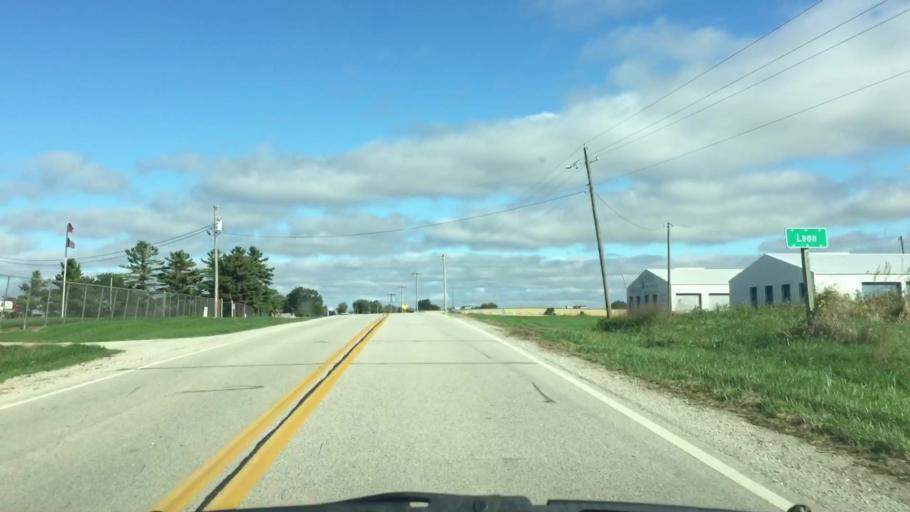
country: US
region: Iowa
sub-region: Decatur County
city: Leon
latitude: 40.7285
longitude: -93.7614
